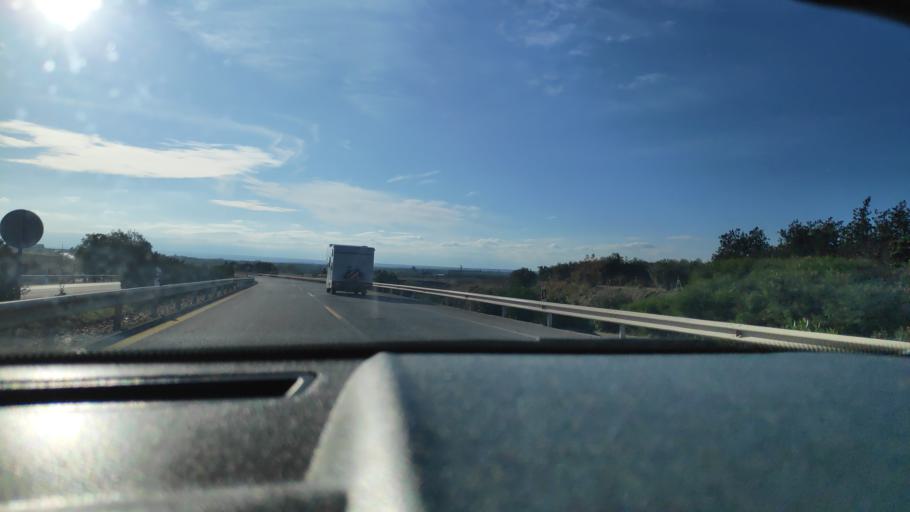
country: ES
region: Andalusia
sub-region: Province of Cordoba
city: La Carlota
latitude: 37.5874
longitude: -4.9861
